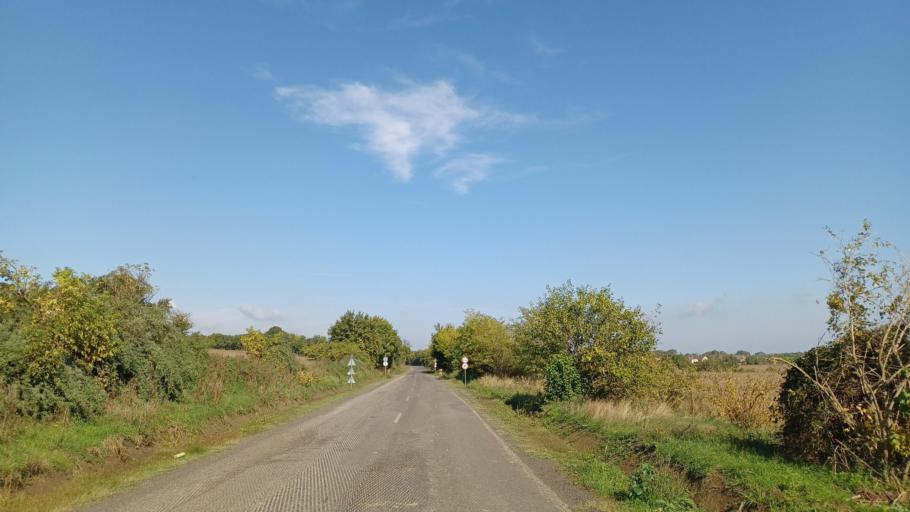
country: HU
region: Tolna
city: Nagydorog
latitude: 46.5943
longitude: 18.5958
